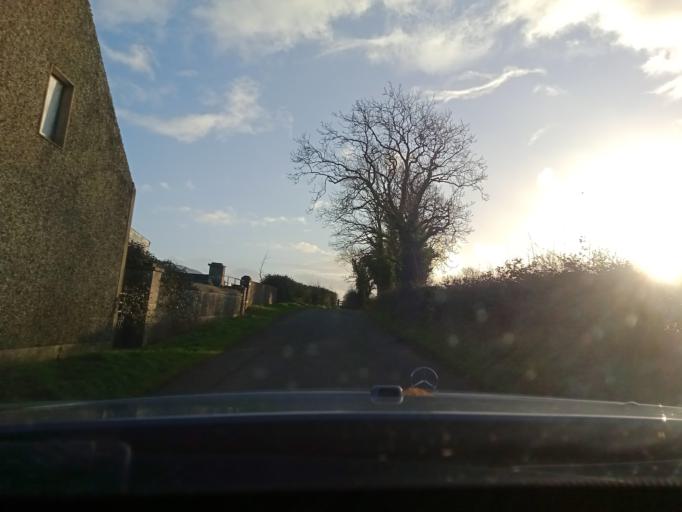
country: IE
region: Leinster
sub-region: Kilkenny
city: Callan
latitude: 52.5337
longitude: -7.3779
